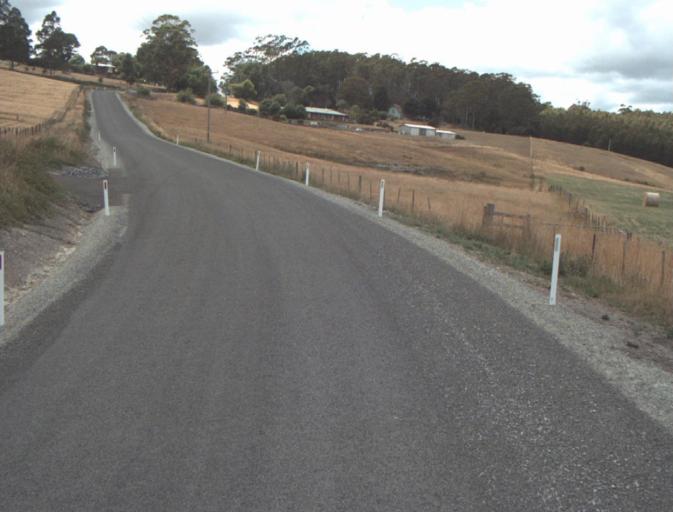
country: AU
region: Tasmania
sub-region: Launceston
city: Mayfield
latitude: -41.1930
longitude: 147.1765
